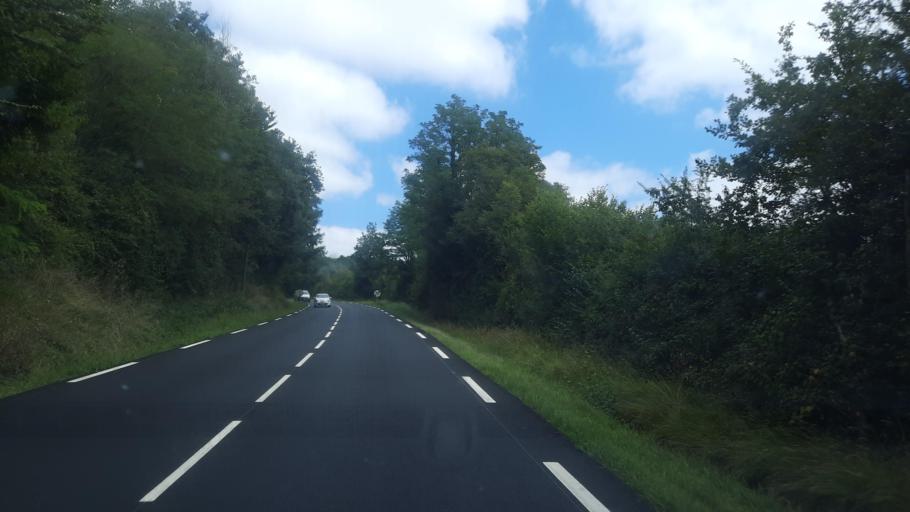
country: FR
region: Midi-Pyrenees
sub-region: Departement de la Haute-Garonne
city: Boulogne-sur-Gesse
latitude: 43.2865
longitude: 0.5481
